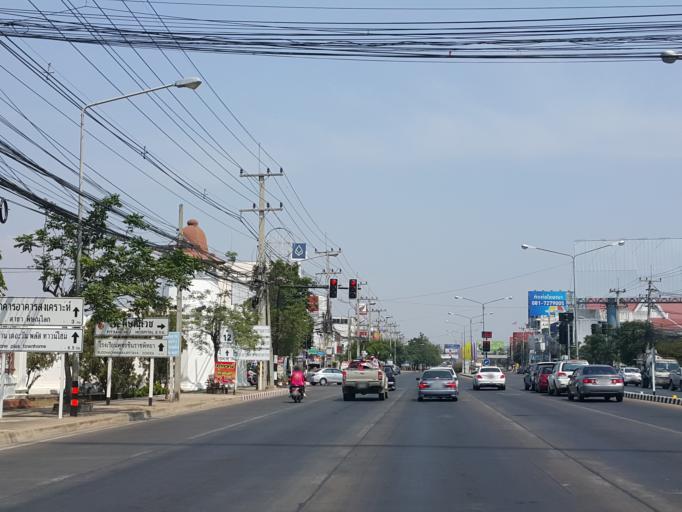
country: TH
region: Phitsanulok
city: Phitsanulok
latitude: 16.8268
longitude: 100.2552
